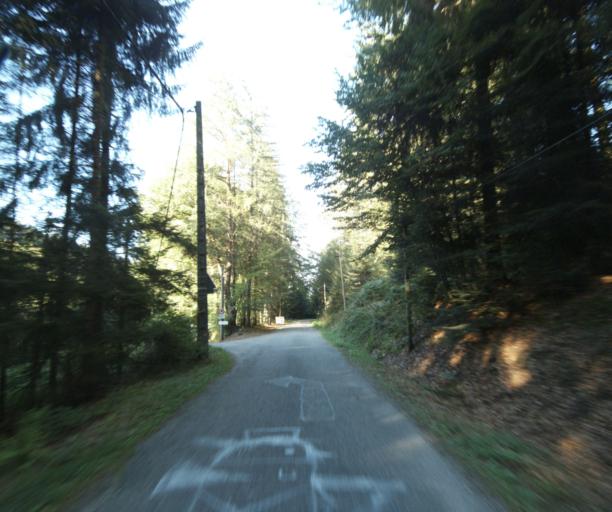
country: FR
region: Lorraine
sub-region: Departement des Vosges
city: Chantraine
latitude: 48.1399
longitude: 6.4268
